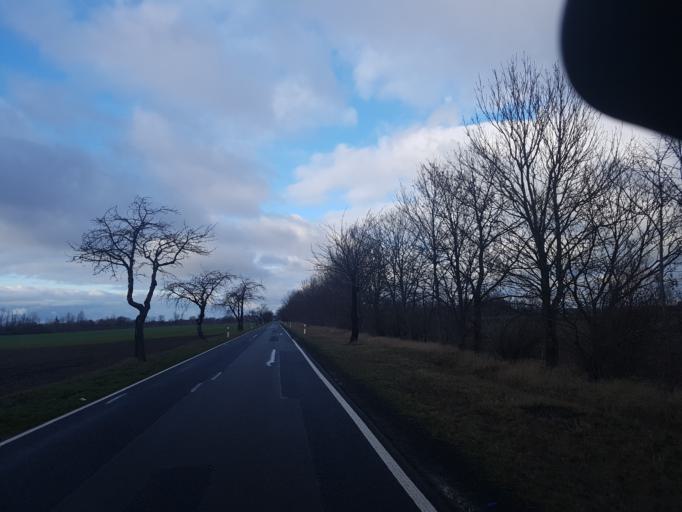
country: DE
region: Brandenburg
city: Muhlberg
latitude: 51.4214
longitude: 13.2306
